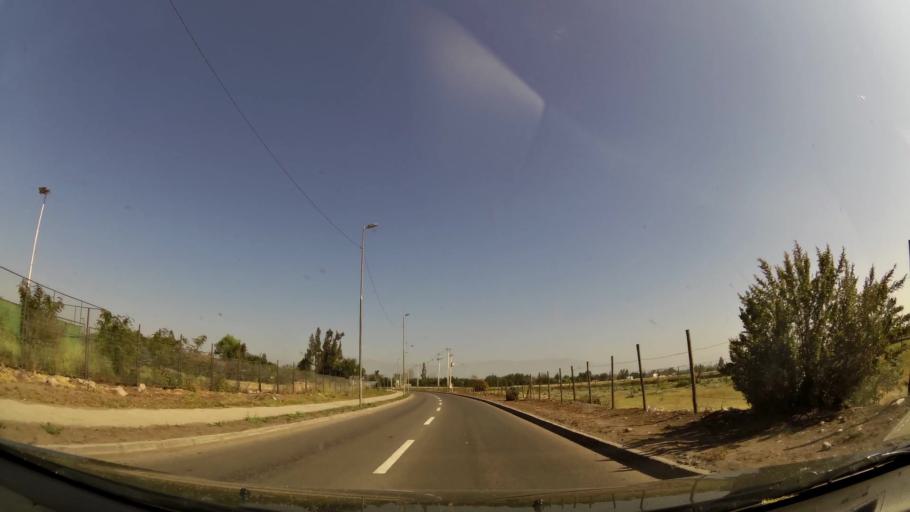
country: CL
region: Santiago Metropolitan
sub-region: Provincia de Chacabuco
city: Chicureo Abajo
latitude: -33.3017
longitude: -70.6863
